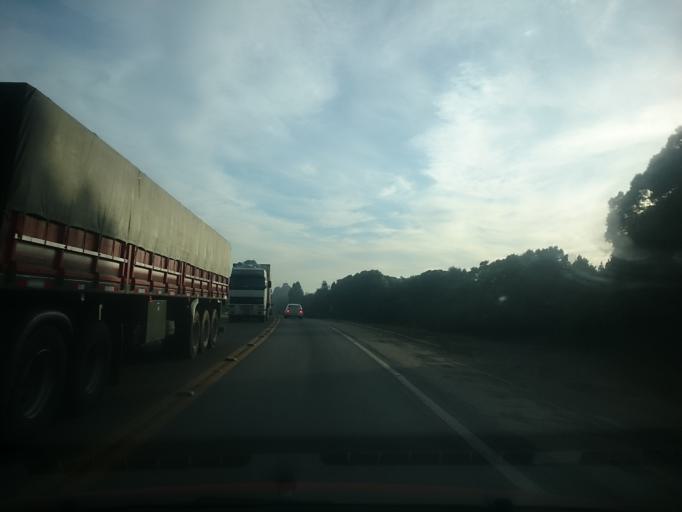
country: BR
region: Rio Grande do Sul
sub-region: Vacaria
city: Estrela
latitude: -28.2643
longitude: -50.7866
